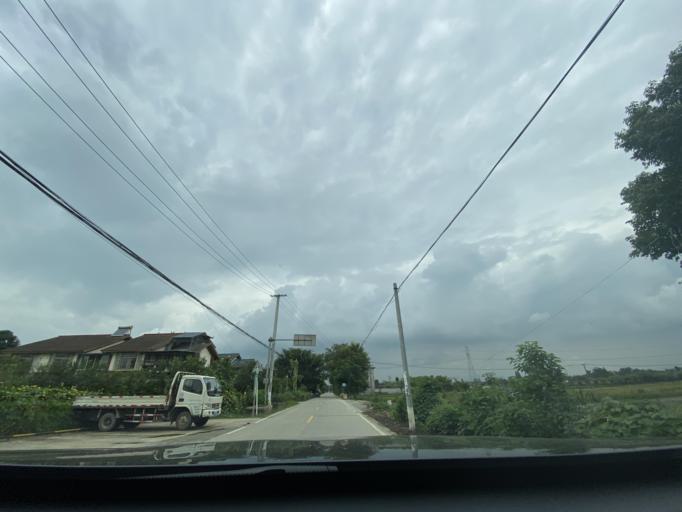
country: CN
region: Sichuan
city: Wujin
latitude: 30.3771
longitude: 103.9682
